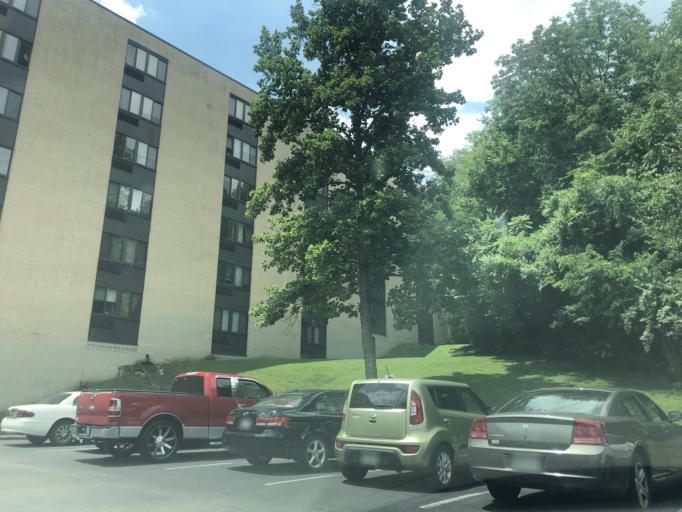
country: US
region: Tennessee
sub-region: Rutherford County
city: La Vergne
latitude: 36.0523
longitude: -86.6500
